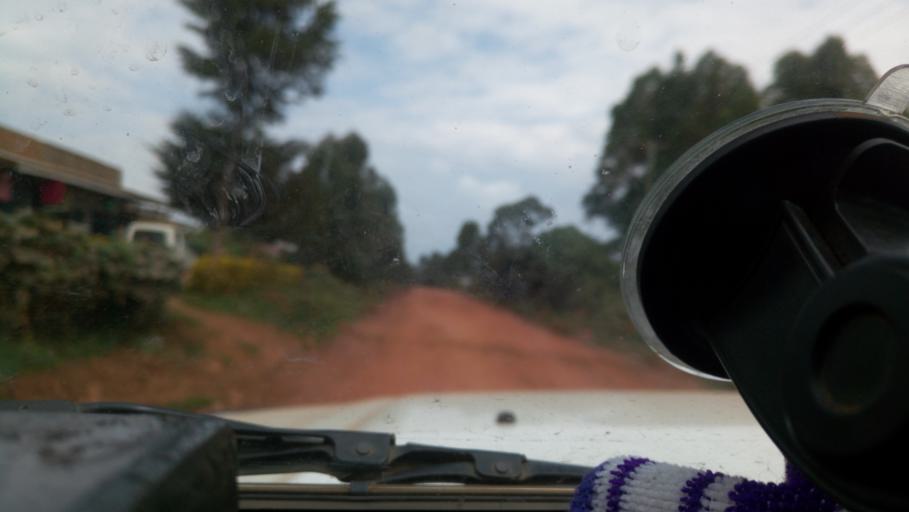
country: KE
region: Kericho
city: Litein
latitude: -0.6001
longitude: 35.1593
